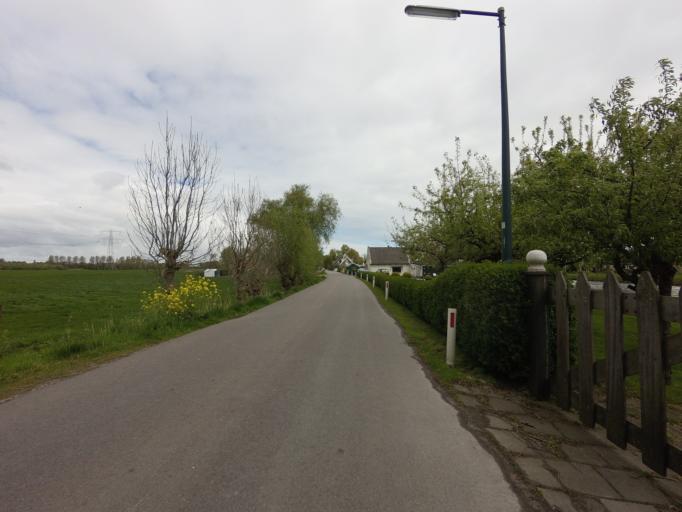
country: NL
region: North Holland
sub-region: Gemeente Amsterdam
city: Driemond
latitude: 52.2954
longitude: 5.0121
